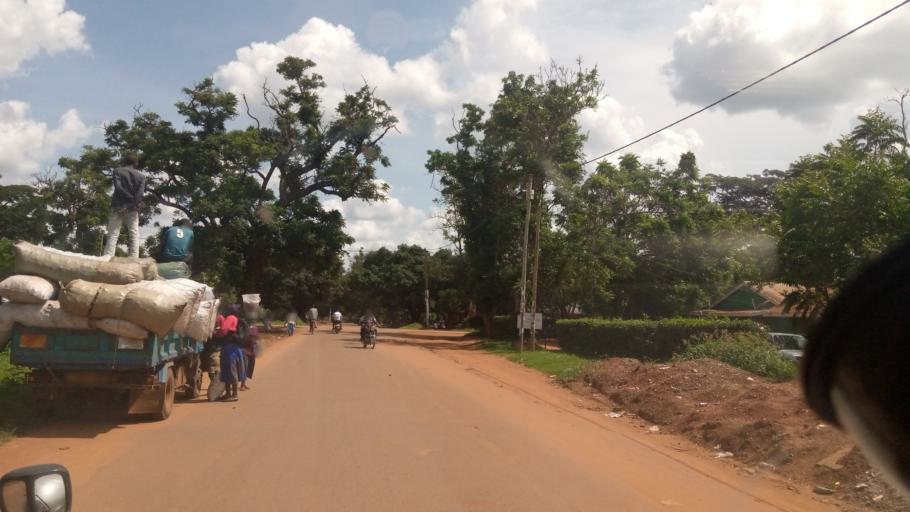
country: UG
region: Northern Region
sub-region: Lira District
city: Lira
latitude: 2.2503
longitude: 32.8992
